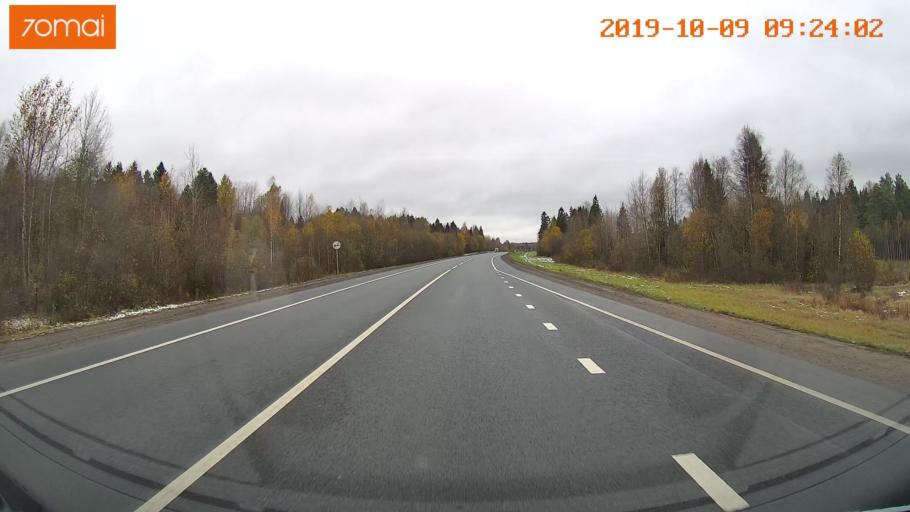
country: RU
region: Vologda
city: Vologda
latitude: 59.0748
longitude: 40.0226
